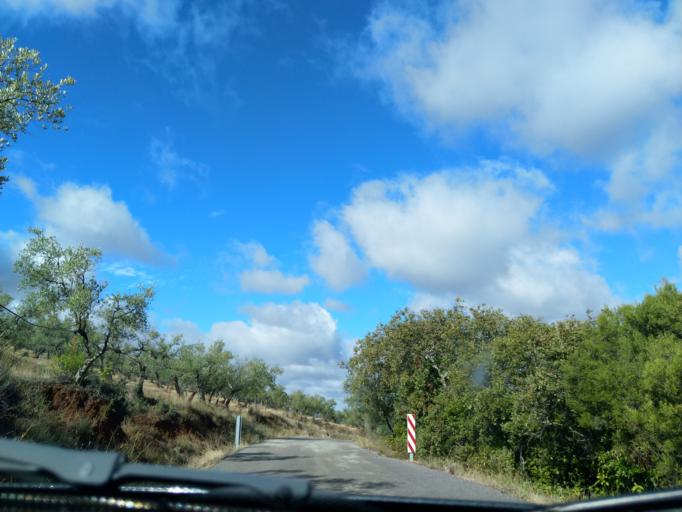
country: ES
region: Extremadura
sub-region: Provincia de Badajoz
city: Reina
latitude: 38.1280
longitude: -5.9231
